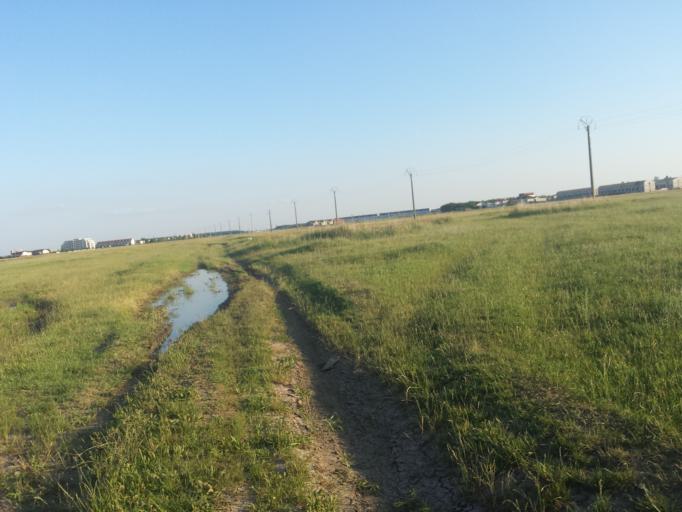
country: RO
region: Ilfov
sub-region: Comuna Tunari
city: Tunari
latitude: 44.5242
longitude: 26.1523
